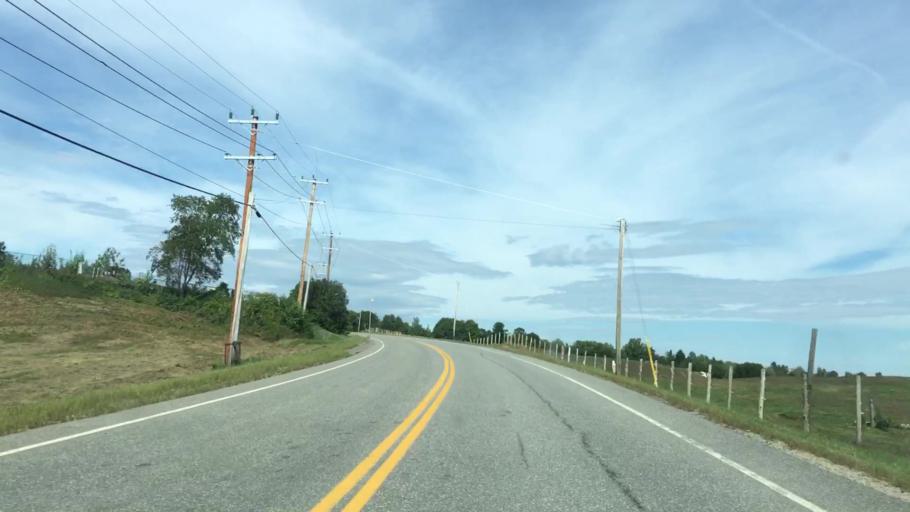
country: US
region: Maine
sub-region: Penobscot County
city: Lincoln
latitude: 45.3969
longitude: -68.5113
